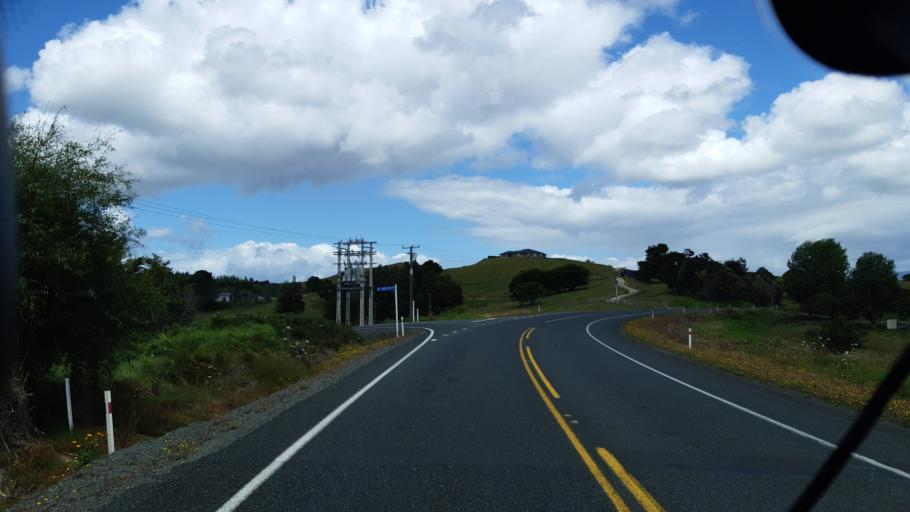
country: NZ
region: Northland
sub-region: Far North District
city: Waimate North
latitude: -35.3016
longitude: 173.5926
